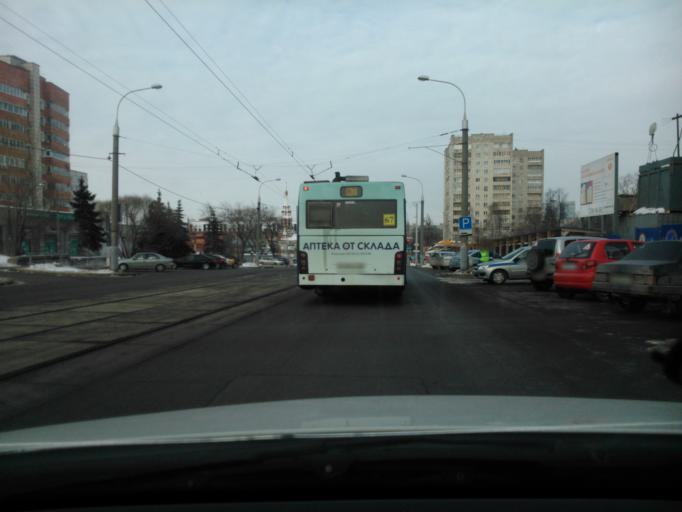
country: RU
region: Perm
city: Perm
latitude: 58.0031
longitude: 56.2233
